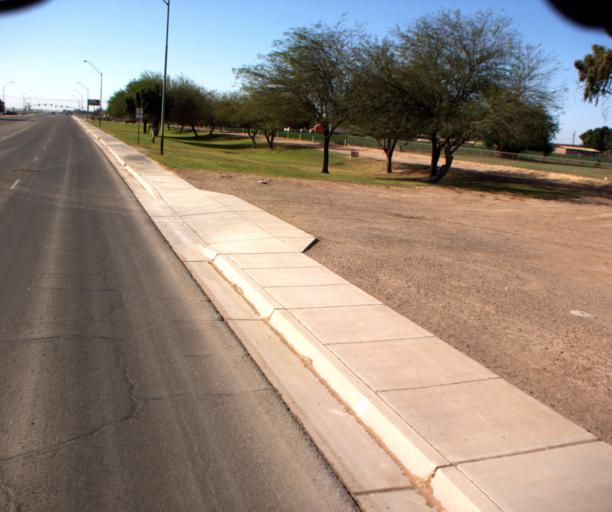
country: US
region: Arizona
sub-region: Yuma County
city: San Luis
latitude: 32.5564
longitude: -114.7849
